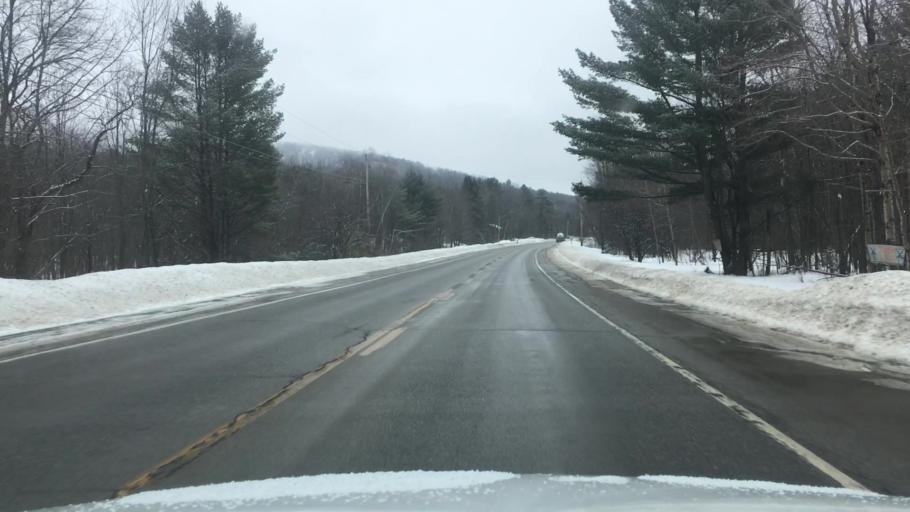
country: US
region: Maine
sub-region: Oxford County
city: Peru
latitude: 44.5876
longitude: -70.3489
